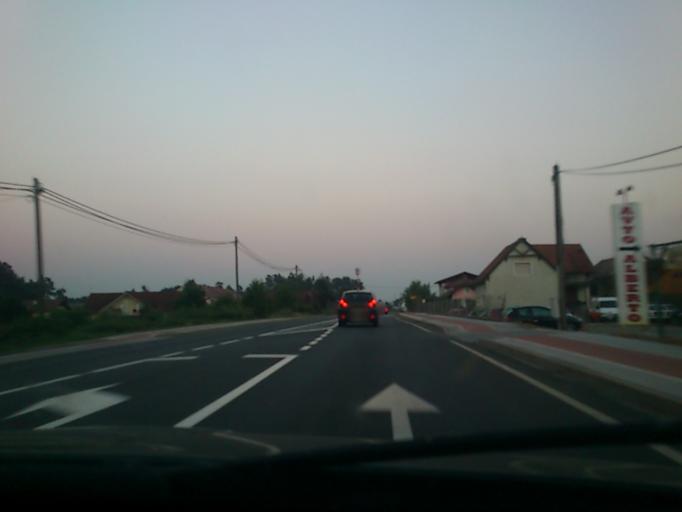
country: SI
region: Miklavz na Dravskem Polju
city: Miklavz na Dravskem Polju
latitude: 46.5142
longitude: 15.6885
